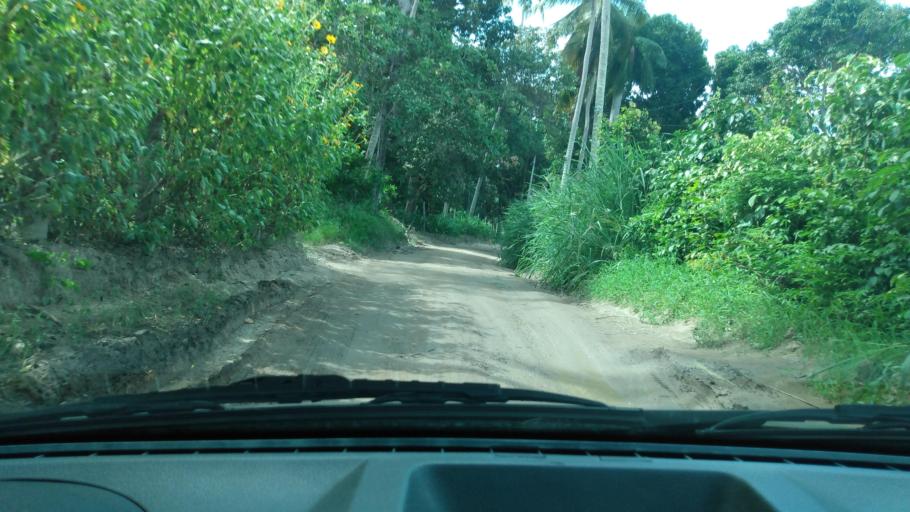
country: BR
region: Pernambuco
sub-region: Cabo De Santo Agostinho
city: Cabo
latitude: -8.3583
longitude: -34.9667
